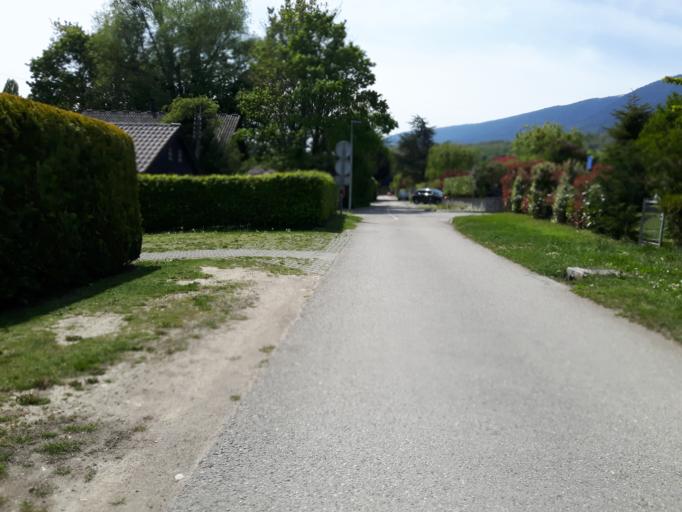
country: CH
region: Neuchatel
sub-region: Boudry District
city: Bevaix
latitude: 46.9241
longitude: 6.8231
